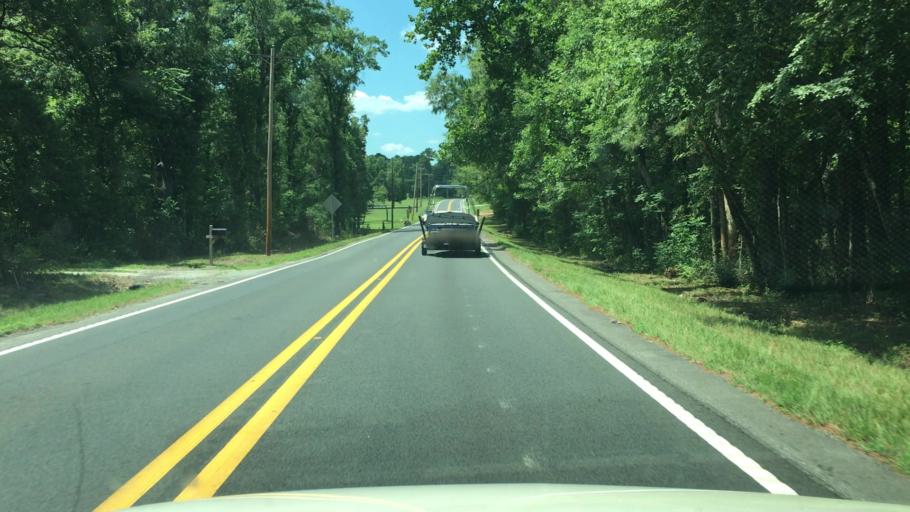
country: US
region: Arkansas
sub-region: Clark County
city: Arkadelphia
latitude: 34.2504
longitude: -93.1201
